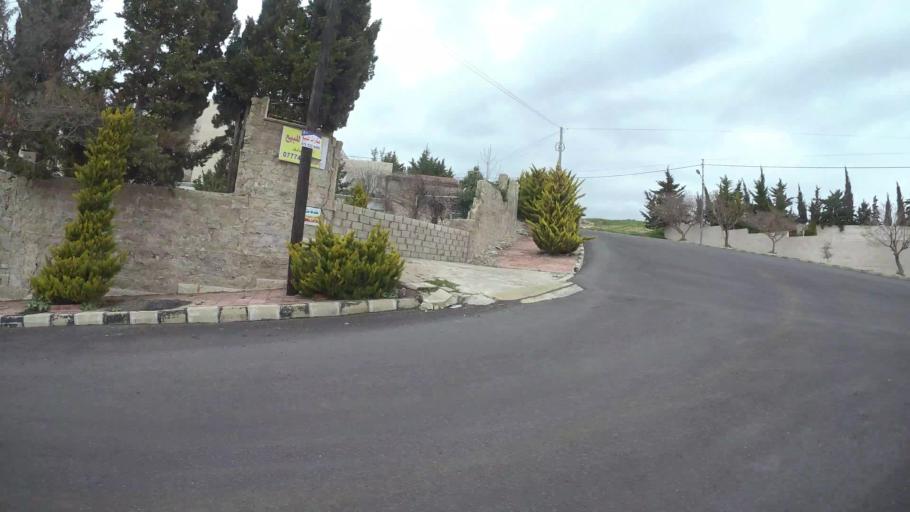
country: JO
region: Amman
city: Wadi as Sir
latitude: 31.9917
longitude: 35.8338
